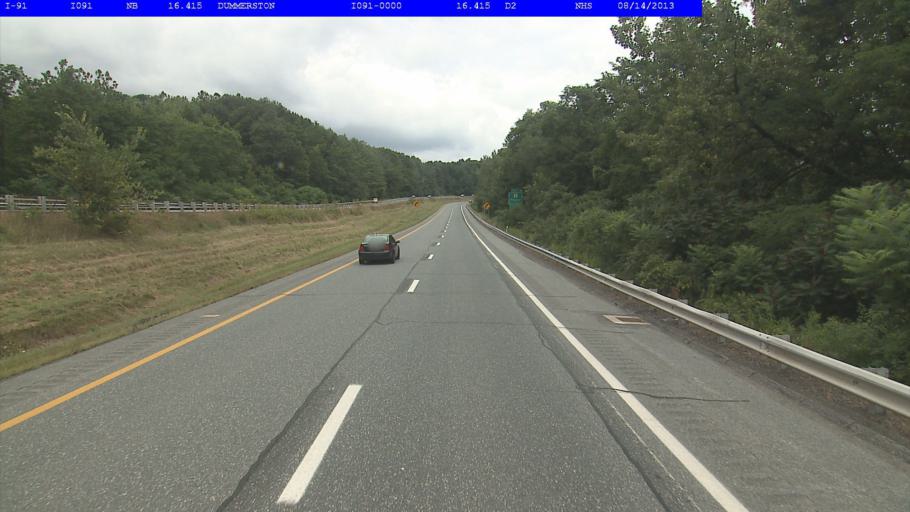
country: US
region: New Hampshire
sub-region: Cheshire County
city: Chesterfield
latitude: 42.9456
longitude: -72.5316
